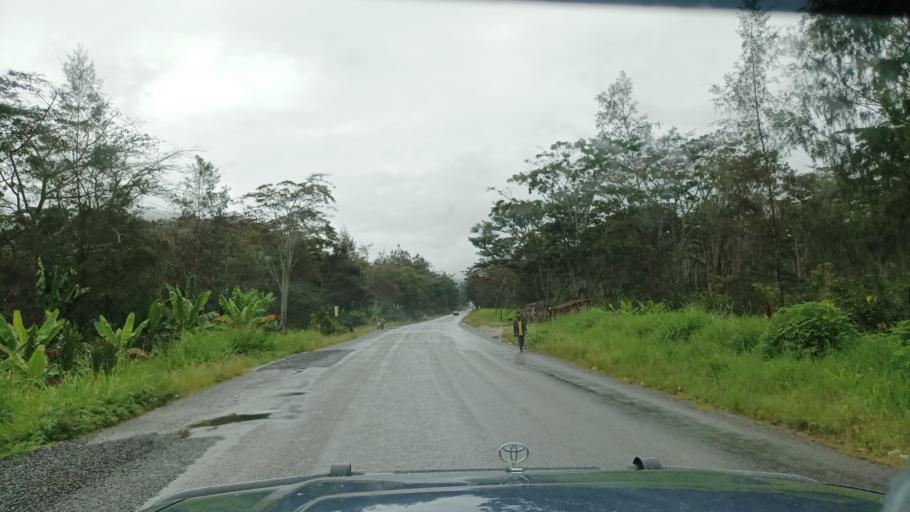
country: PG
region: Western Highlands
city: Rauna
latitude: -5.8333
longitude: 144.3468
